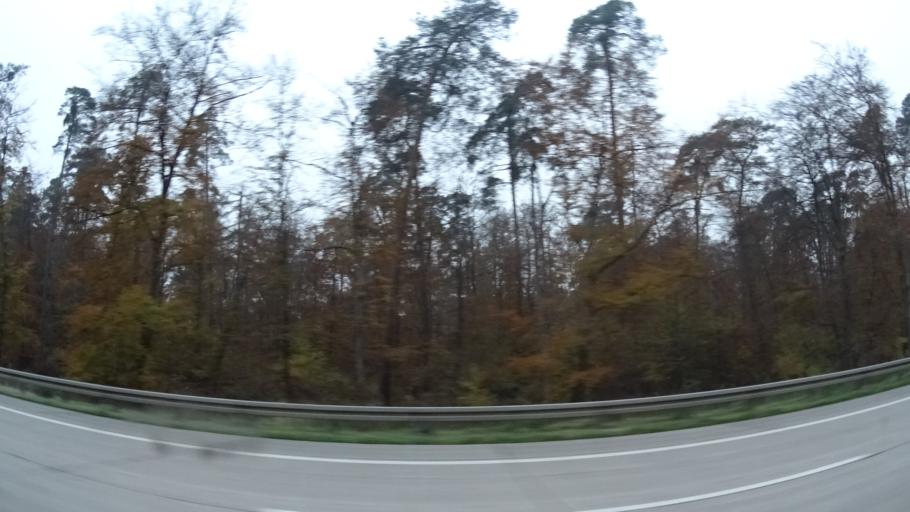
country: DE
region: Baden-Wuerttemberg
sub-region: Karlsruhe Region
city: Sankt Leon-Rot
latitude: 49.2408
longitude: 8.6013
